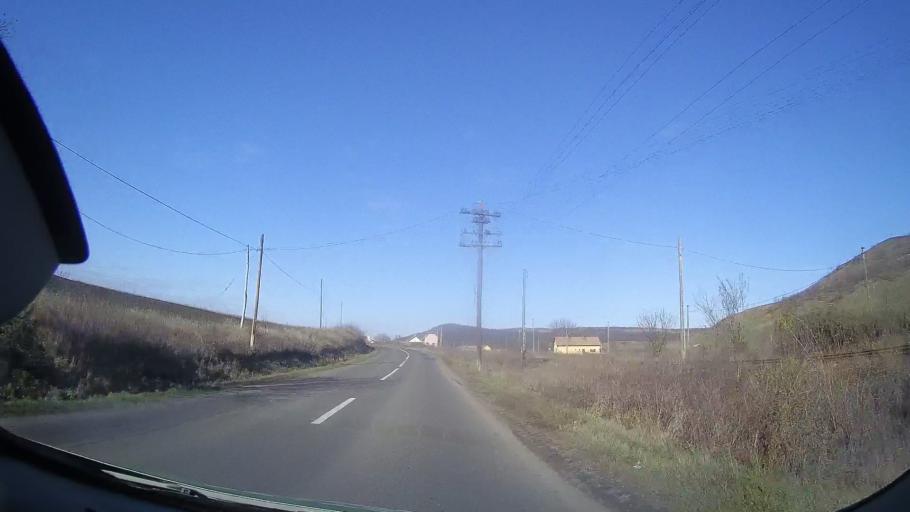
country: RO
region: Mures
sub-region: Comuna Mihesu de Campie
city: Mihesu de Campie
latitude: 46.6587
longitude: 24.1765
